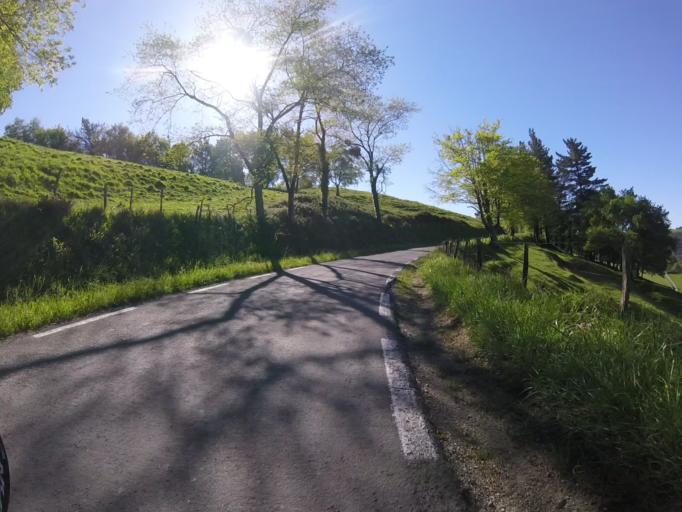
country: ES
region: Basque Country
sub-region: Provincia de Guipuzcoa
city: Aizarnazabal
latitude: 43.2160
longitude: -2.2096
